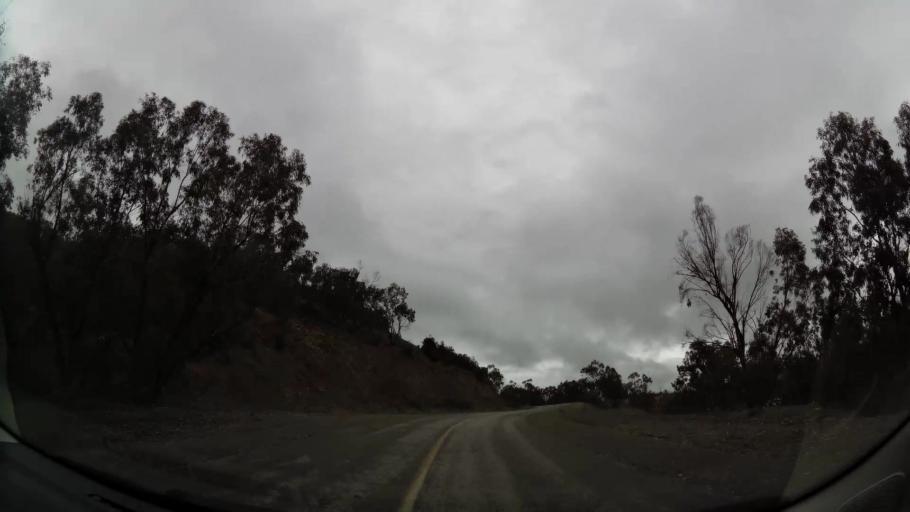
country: MA
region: Taza-Al Hoceima-Taounate
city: Imzourene
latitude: 34.9463
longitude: -3.8071
